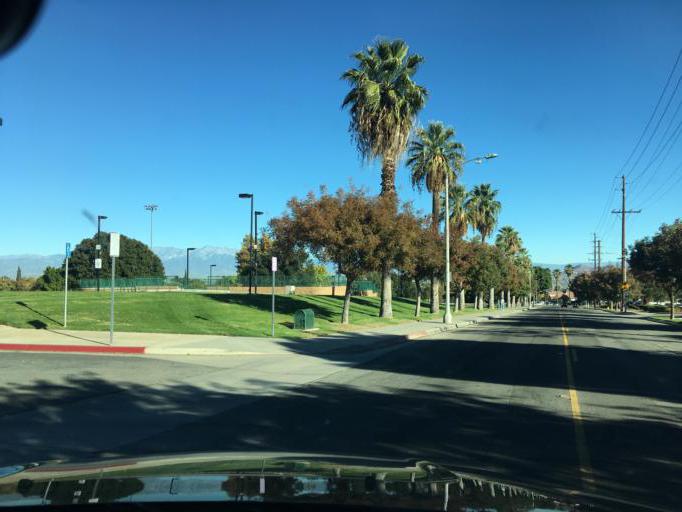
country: US
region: California
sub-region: Riverside County
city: Corona
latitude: 33.8521
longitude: -117.5575
